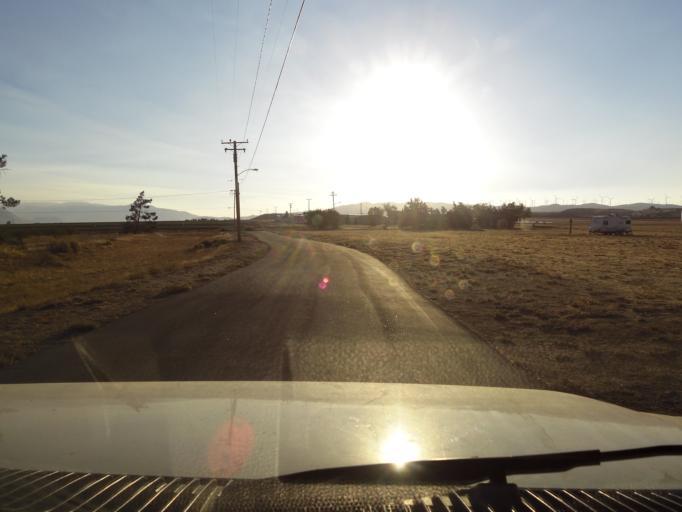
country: US
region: California
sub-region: Kern County
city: Tehachapi
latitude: 35.1027
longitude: -118.4252
